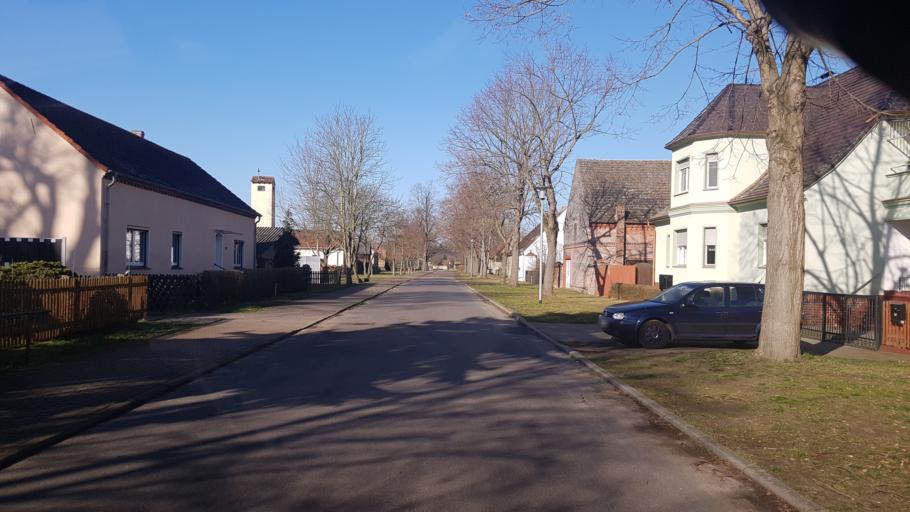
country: DE
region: Brandenburg
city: Luckau
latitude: 51.8345
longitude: 13.8005
